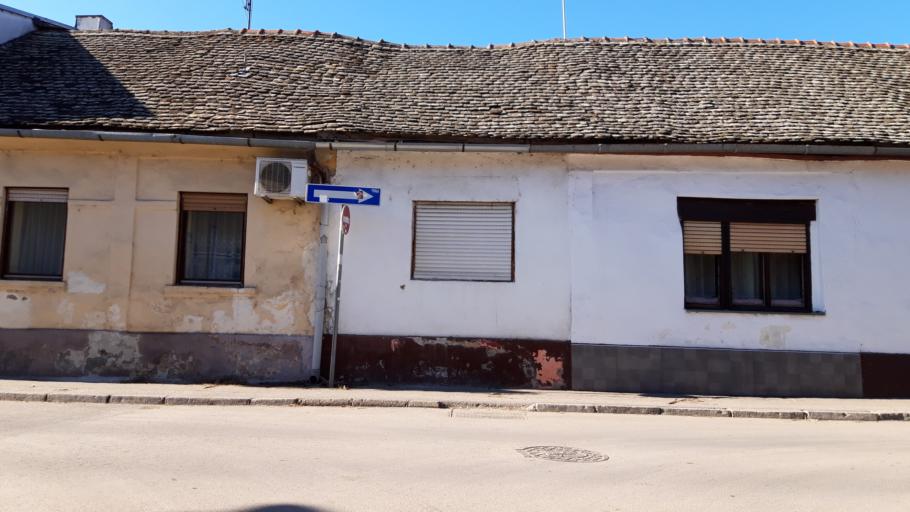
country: RS
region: Autonomna Pokrajina Vojvodina
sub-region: Juznobacki Okrug
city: Novi Sad
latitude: 45.2605
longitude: 19.8468
